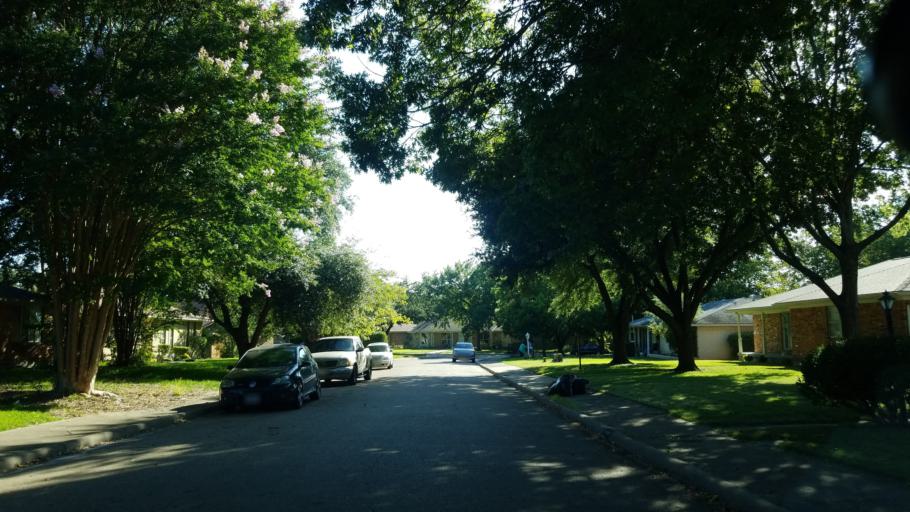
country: US
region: Texas
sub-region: Dallas County
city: Highland Park
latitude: 32.7898
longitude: -96.7094
